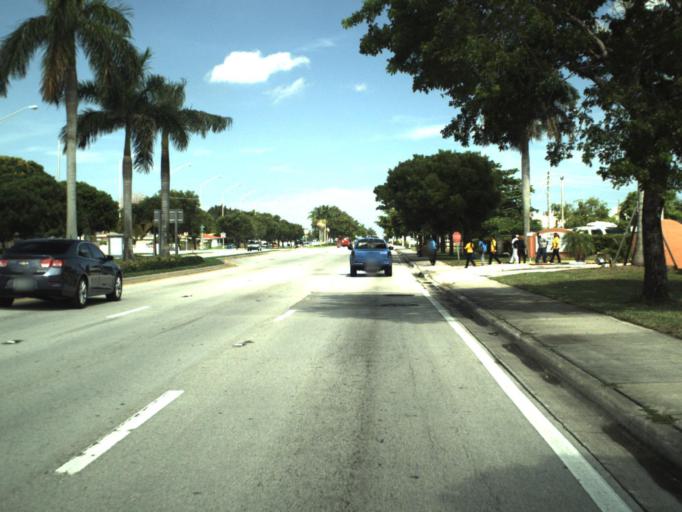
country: US
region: Florida
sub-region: Miami-Dade County
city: Carol City
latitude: 25.9406
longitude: -80.2519
